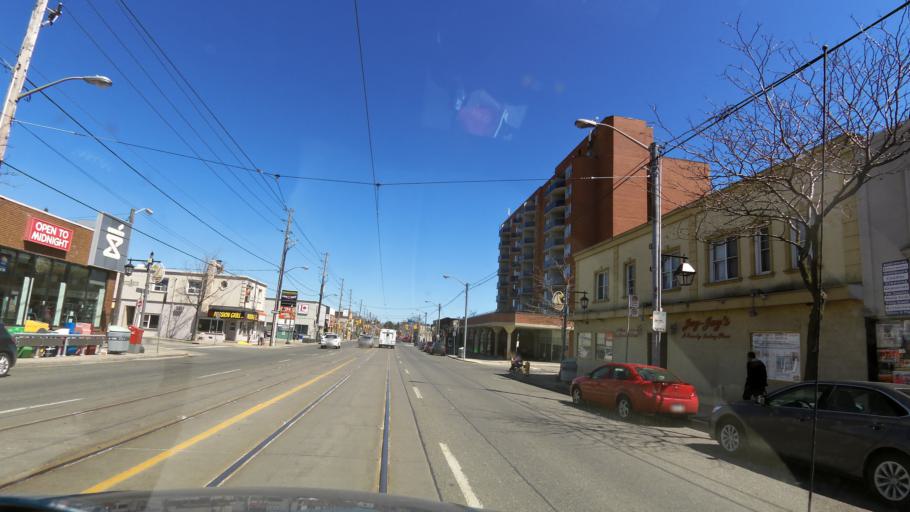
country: CA
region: Ontario
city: Etobicoke
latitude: 43.6014
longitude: -79.5024
